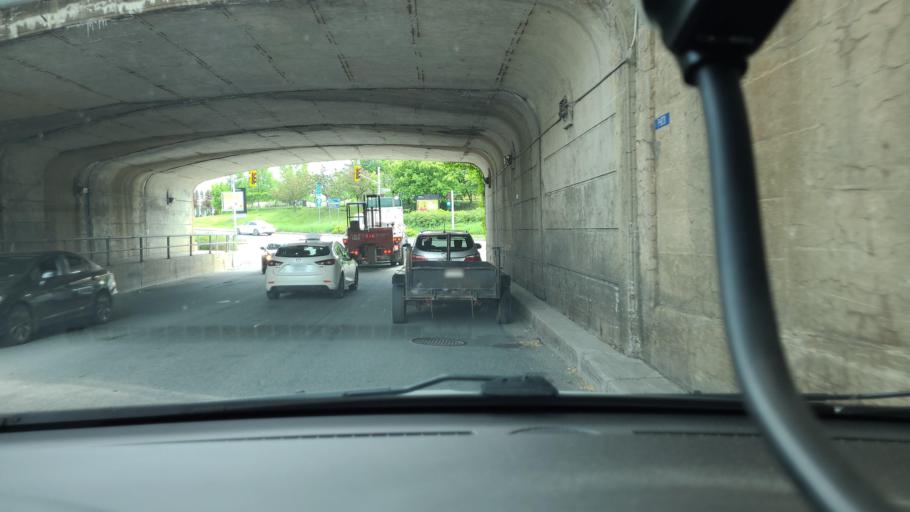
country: CA
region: Quebec
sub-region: Monteregie
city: Saint-Hyacinthe
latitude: 45.6274
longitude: -72.9512
